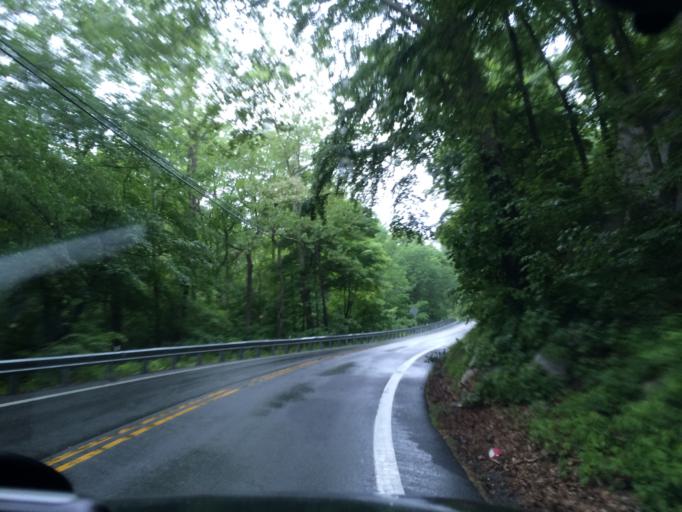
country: US
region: Maryland
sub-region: Frederick County
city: Thurmont
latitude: 39.6492
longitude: -77.4305
